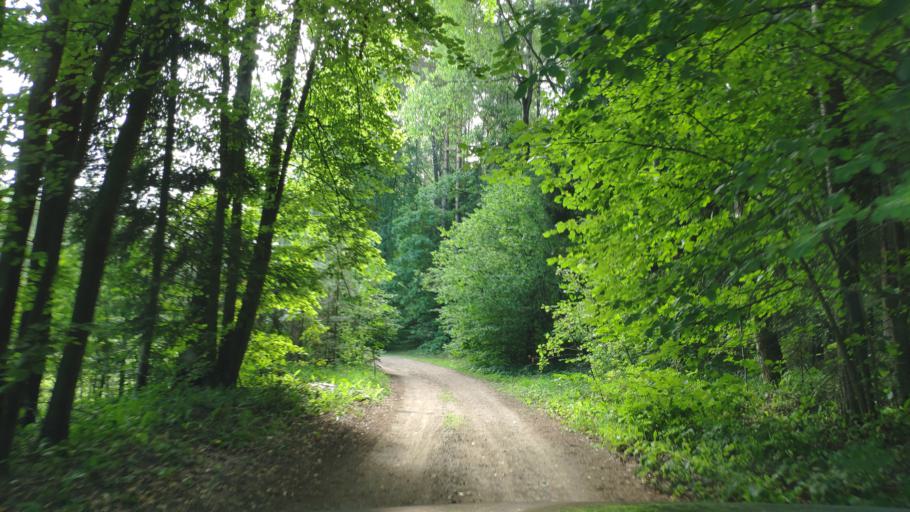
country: BY
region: Minsk
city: Khatsyezhyna
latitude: 53.9624
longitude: 27.3018
